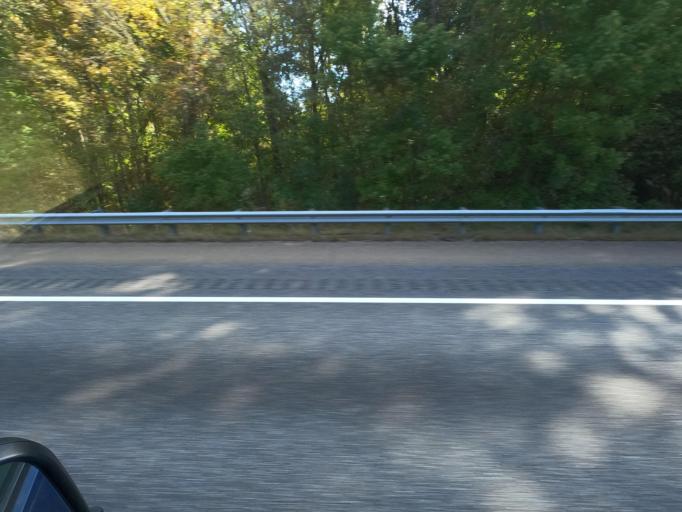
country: US
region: Tennessee
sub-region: Haywood County
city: Brownsville
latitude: 35.5304
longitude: -89.2575
